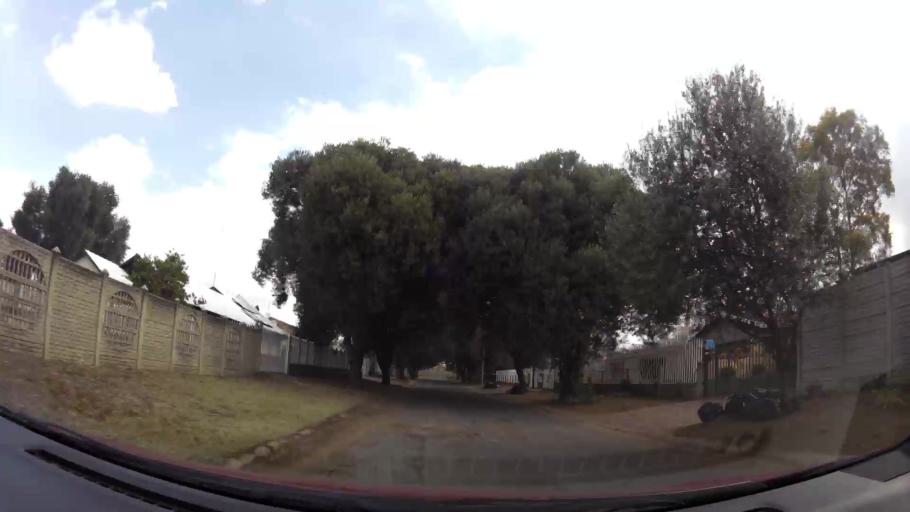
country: ZA
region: Gauteng
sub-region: Sedibeng District Municipality
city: Vanderbijlpark
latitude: -26.7113
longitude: 27.8381
